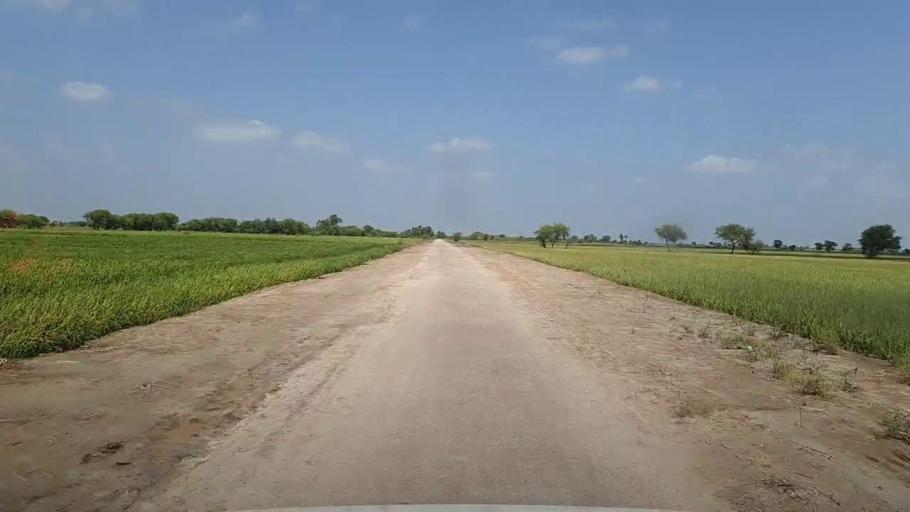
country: PK
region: Sindh
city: Kario
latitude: 24.6888
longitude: 68.5881
